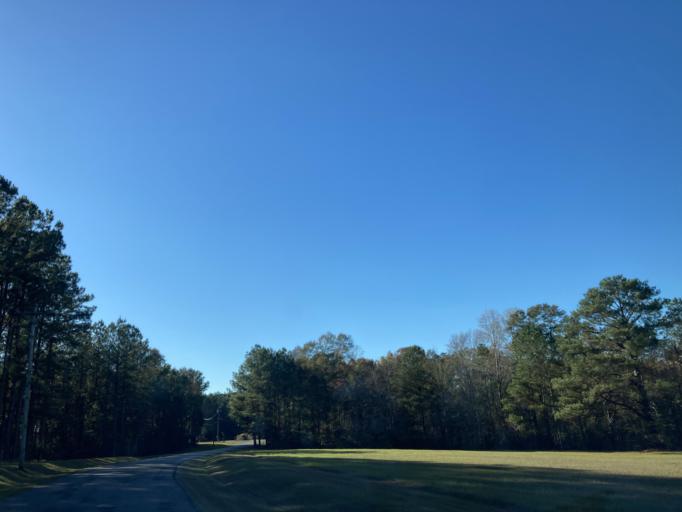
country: US
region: Mississippi
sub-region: Lamar County
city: Sumrall
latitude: 31.3657
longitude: -89.5673
